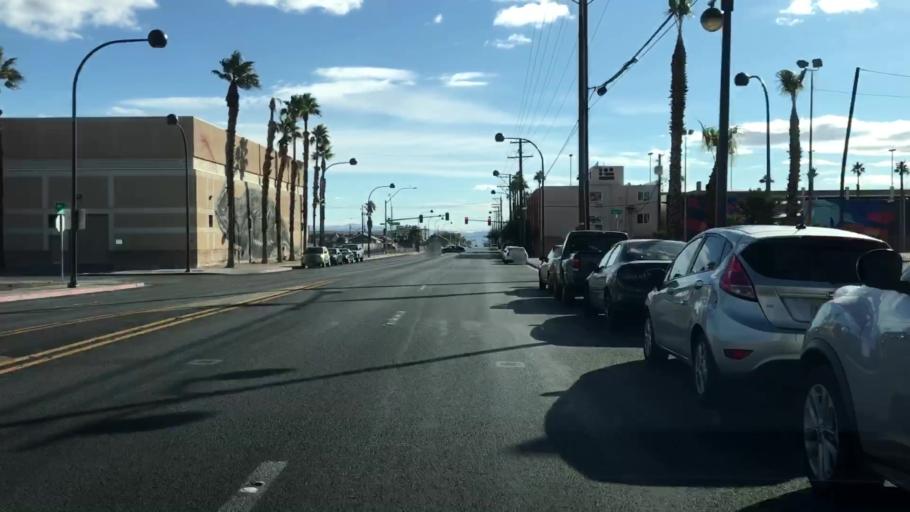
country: US
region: Nevada
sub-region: Clark County
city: Las Vegas
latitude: 36.1712
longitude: -115.1386
